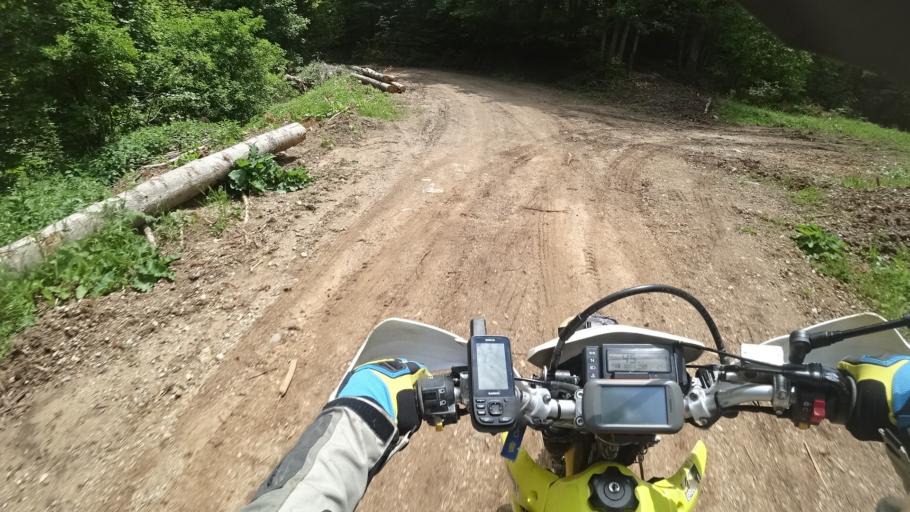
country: HR
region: Zadarska
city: Gracac
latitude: 44.4867
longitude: 15.8751
